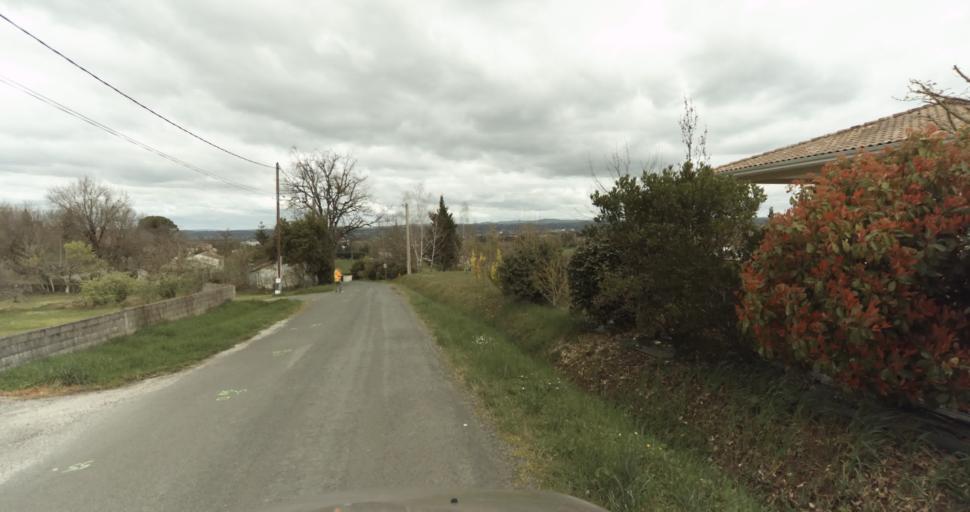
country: FR
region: Midi-Pyrenees
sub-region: Departement du Tarn
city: Puygouzon
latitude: 43.9044
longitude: 2.1673
